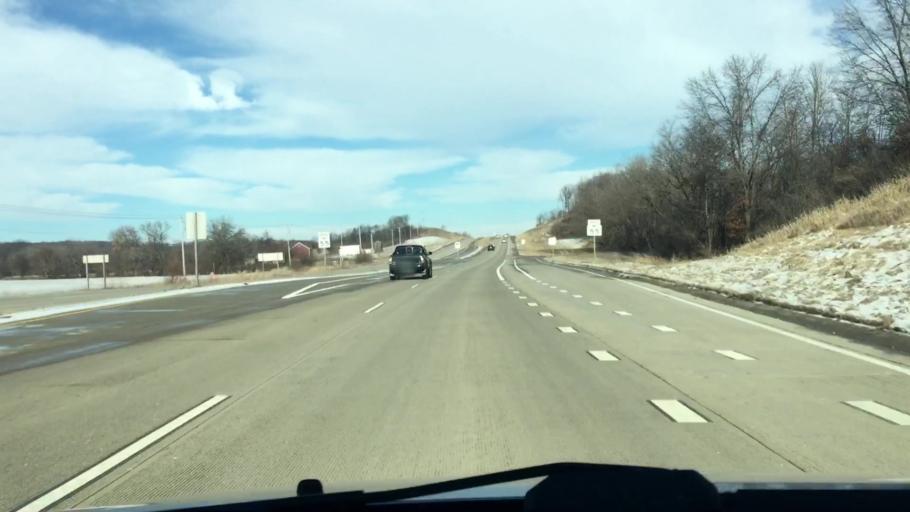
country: US
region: Wisconsin
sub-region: Waukesha County
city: Mukwonago
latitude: 42.9025
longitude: -88.3453
